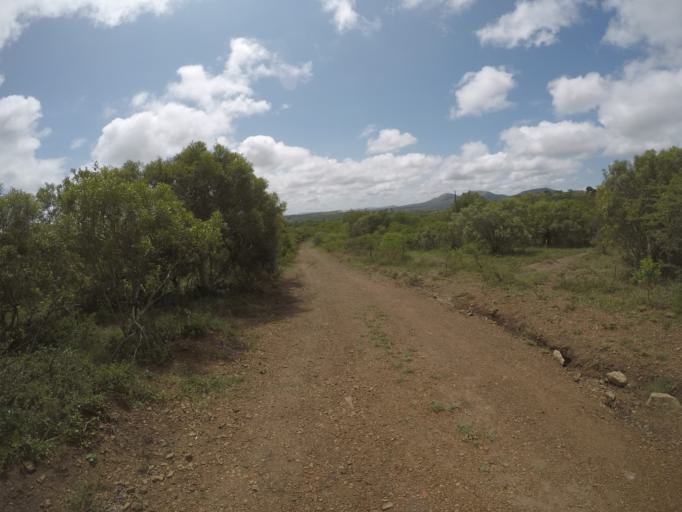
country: ZA
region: KwaZulu-Natal
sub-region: uThungulu District Municipality
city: Empangeni
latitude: -28.5733
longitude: 31.8295
